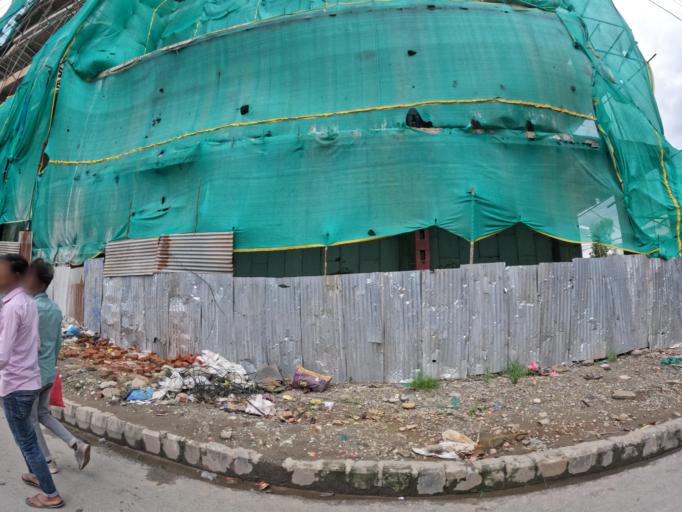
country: NP
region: Central Region
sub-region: Bagmati Zone
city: Kathmandu
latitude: 27.7356
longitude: 85.3177
